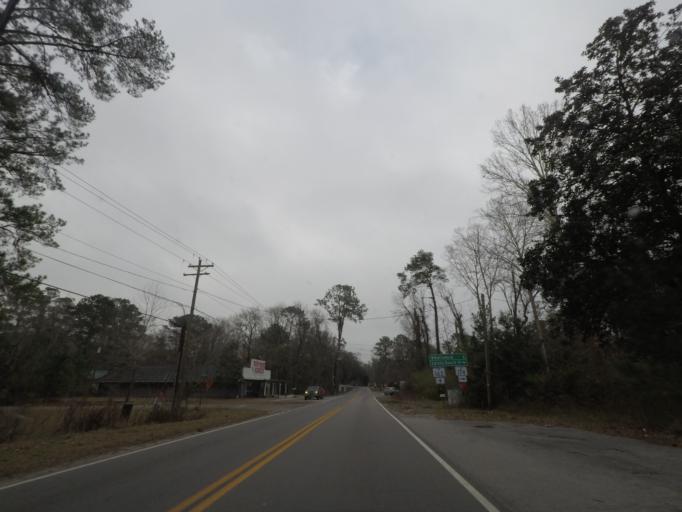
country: US
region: South Carolina
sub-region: Charleston County
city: Ravenel
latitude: 32.7212
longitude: -80.3491
